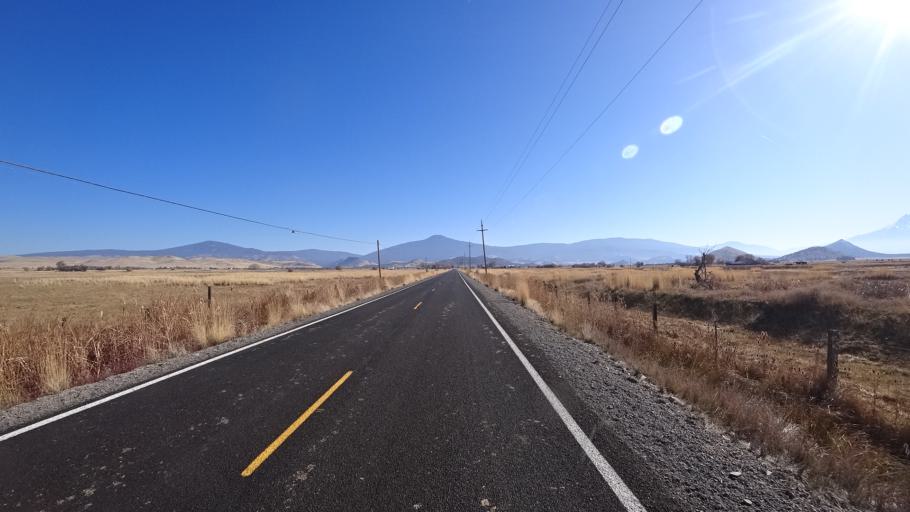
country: US
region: California
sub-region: Siskiyou County
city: Montague
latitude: 41.7114
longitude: -122.4278
